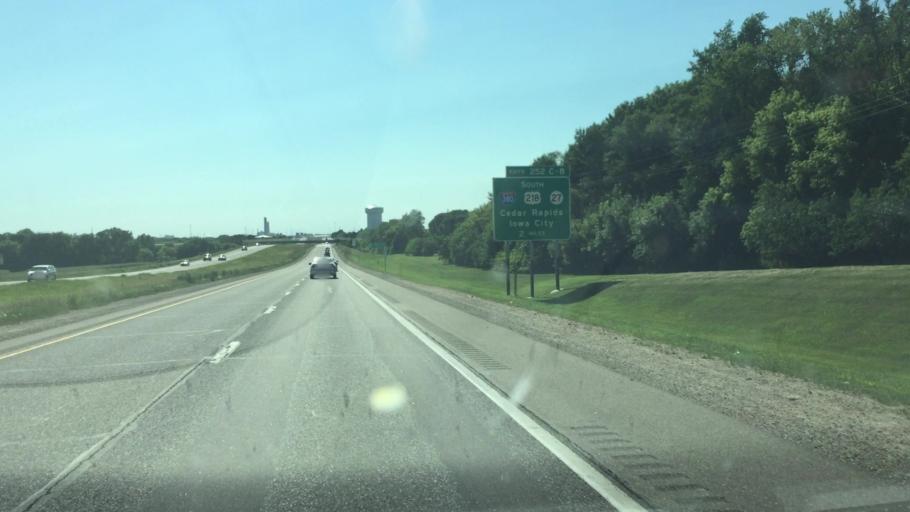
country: US
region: Iowa
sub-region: Linn County
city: Ely
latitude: 41.9266
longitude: -91.6254
